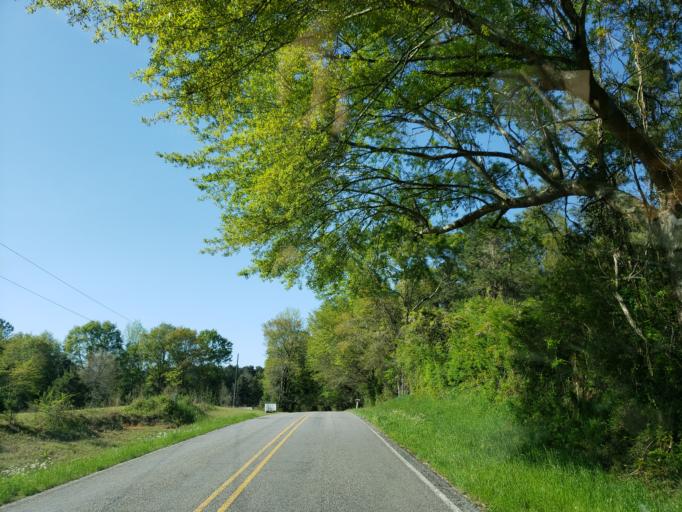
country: US
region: Mississippi
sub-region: Forrest County
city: Rawls Springs
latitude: 31.5328
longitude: -89.3602
